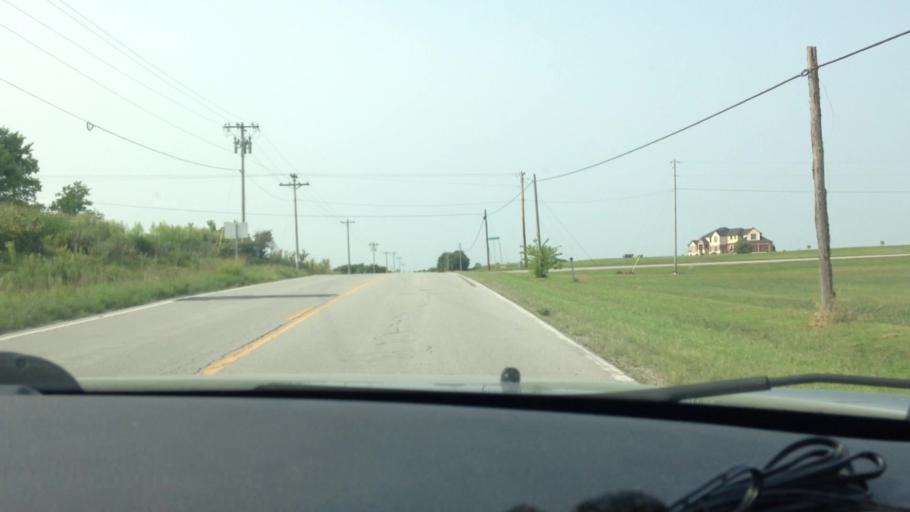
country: US
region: Missouri
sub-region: Platte County
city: Platte City
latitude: 39.4180
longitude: -94.7962
